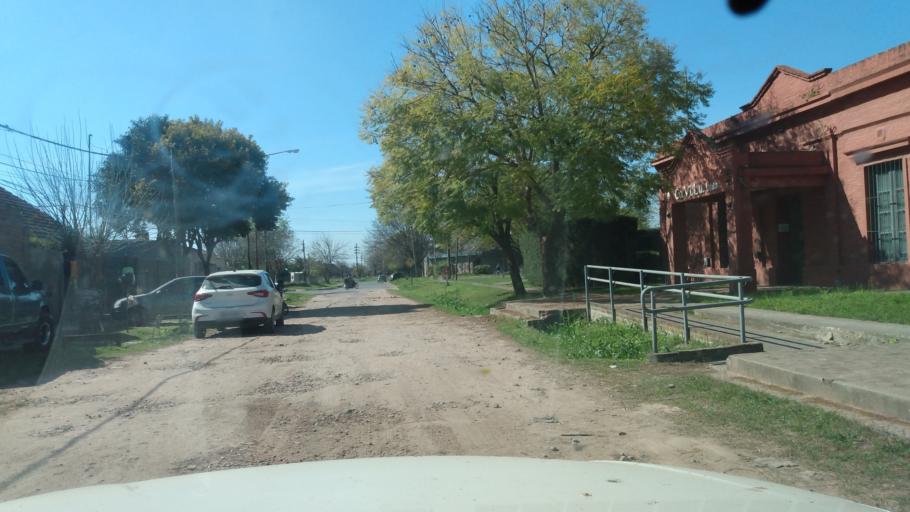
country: AR
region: Buenos Aires
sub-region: Partido de Lujan
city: Lujan
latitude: -34.5781
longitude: -59.1016
